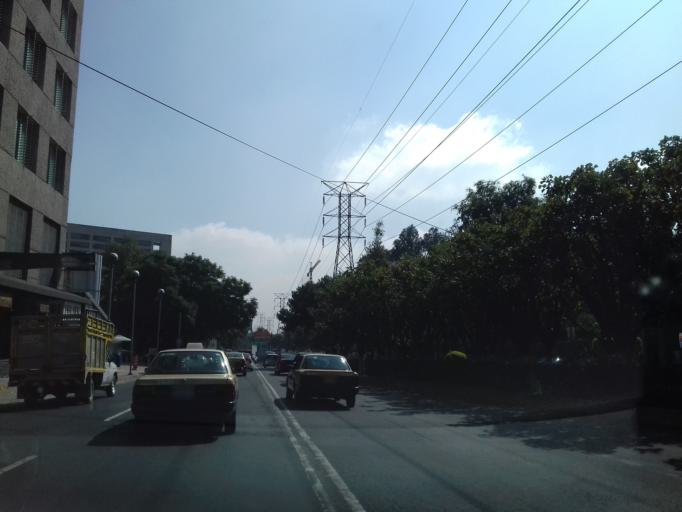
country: MX
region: Mexico City
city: Magdalena Contreras
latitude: 19.3328
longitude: -99.2040
